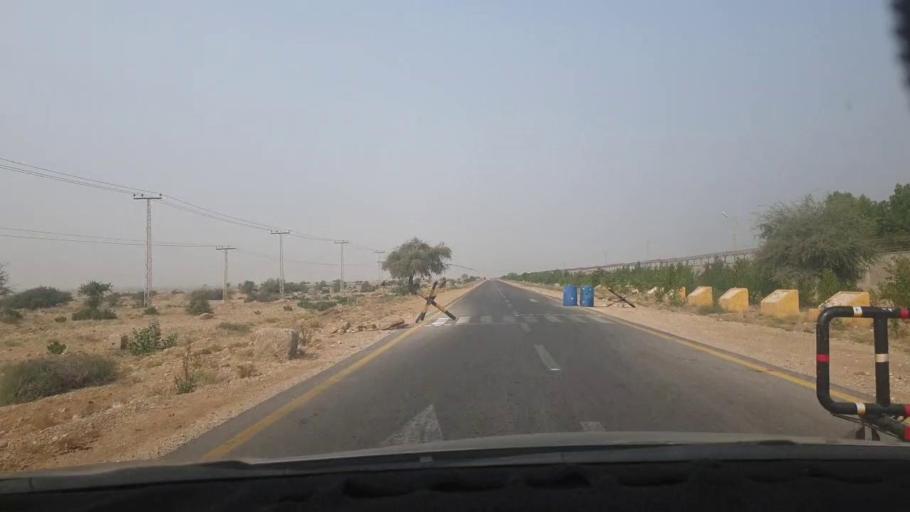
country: PK
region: Sindh
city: Jamshoro
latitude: 25.5446
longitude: 68.3204
